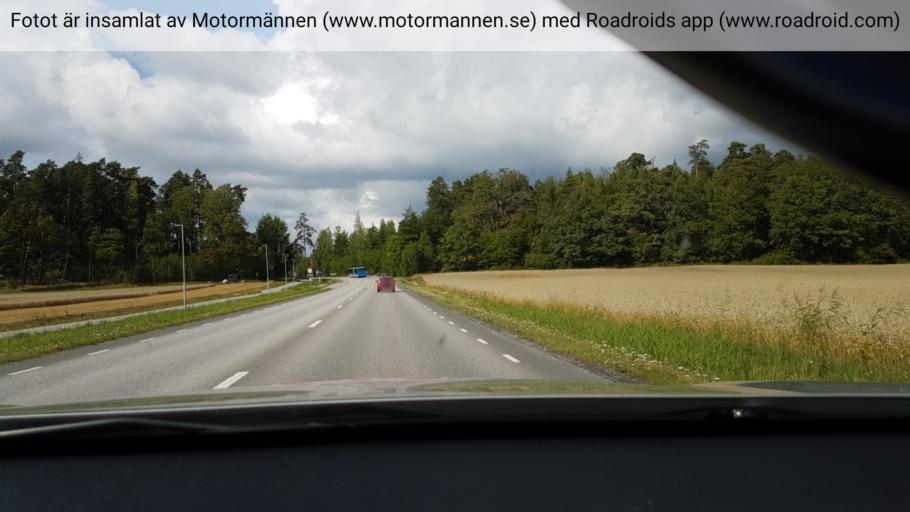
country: SE
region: Stockholm
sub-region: Ekero Kommun
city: Ekeroe
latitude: 59.2986
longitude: 17.8105
